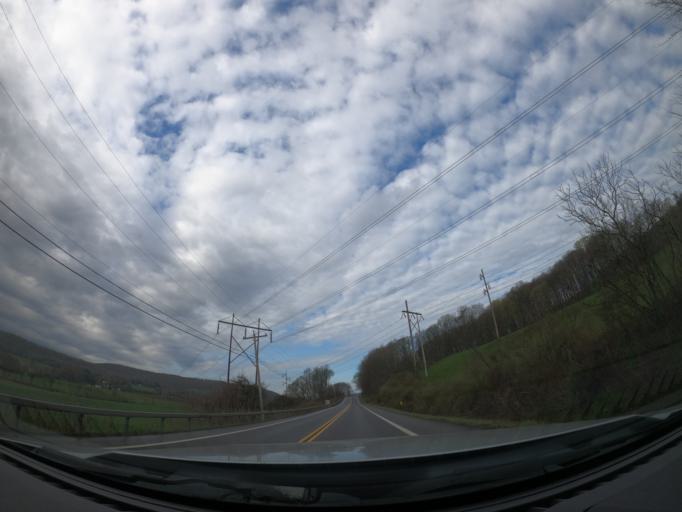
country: US
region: New York
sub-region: Cortland County
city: McGraw
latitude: 42.6795
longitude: -76.0688
